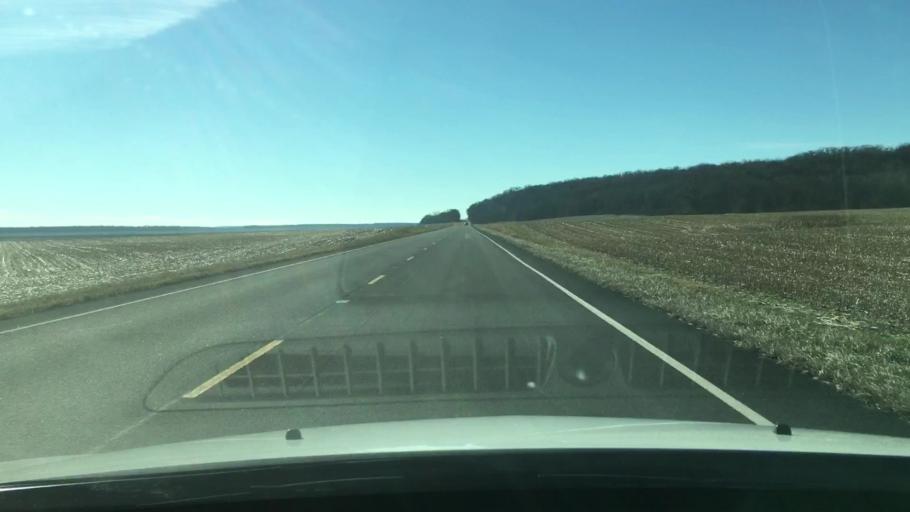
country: US
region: Illinois
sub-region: Fulton County
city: Canton
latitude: 40.4427
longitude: -89.9657
